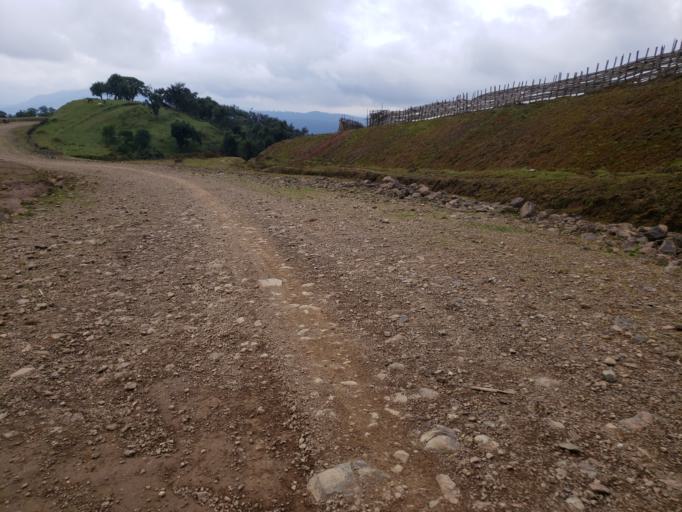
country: ET
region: Oromiya
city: Dodola
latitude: 6.6960
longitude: 39.3688
